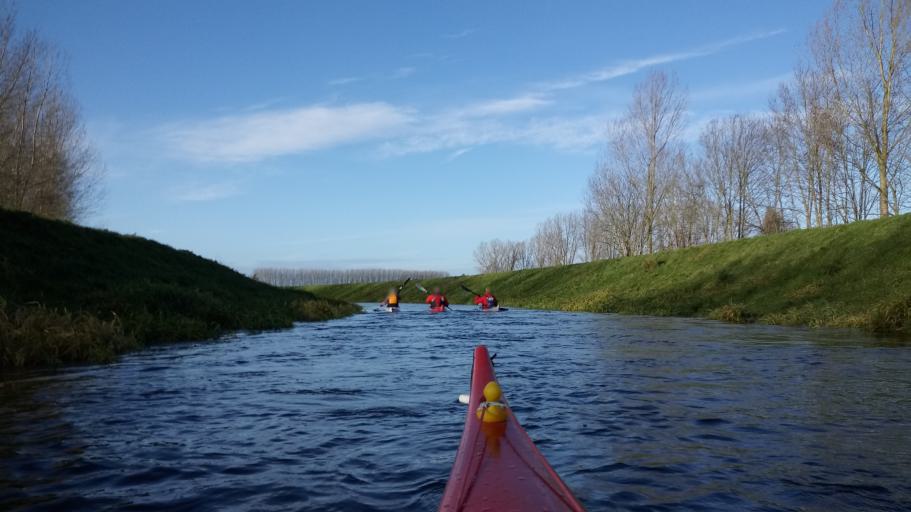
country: NL
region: Gelderland
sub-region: Gemeente Bronckhorst
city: Baak
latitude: 52.0975
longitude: 6.2357
